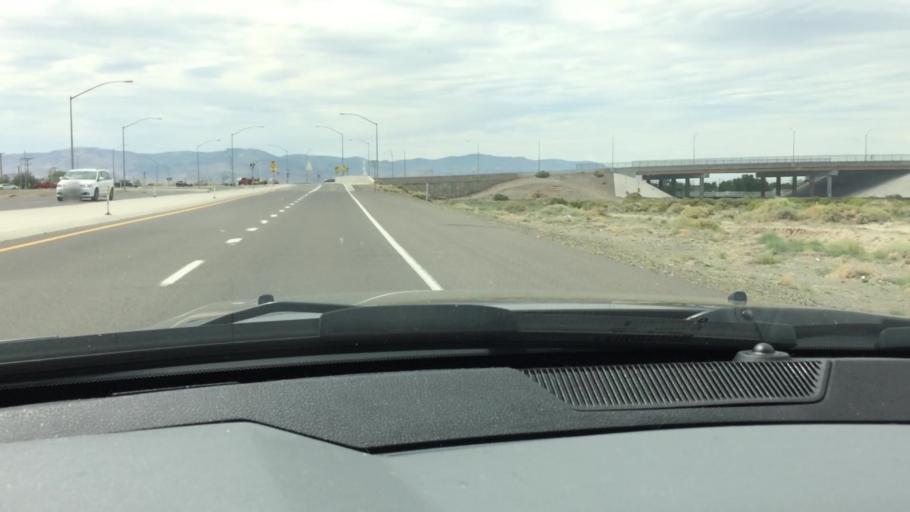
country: US
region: Nevada
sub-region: Lyon County
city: Fernley
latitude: 39.6028
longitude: -119.2245
